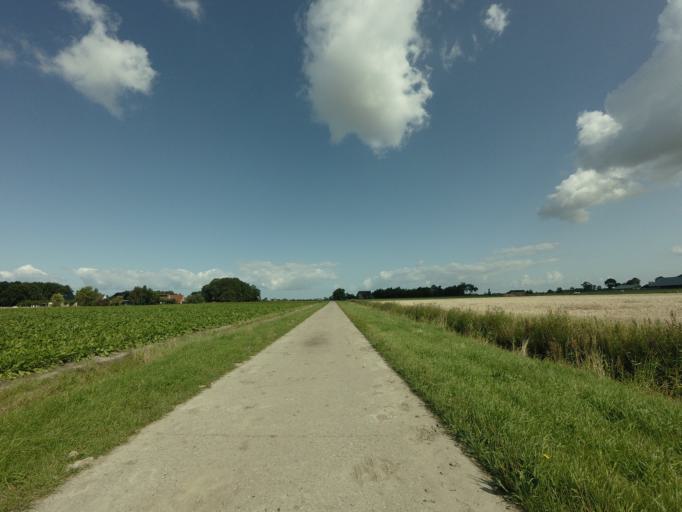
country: NL
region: Friesland
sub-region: Gemeente Het Bildt
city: Sint Jacobiparochie
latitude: 53.2703
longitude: 5.6158
